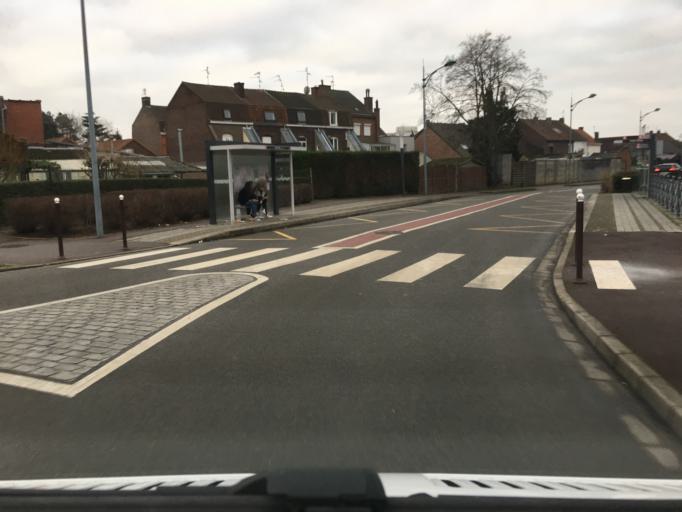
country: FR
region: Nord-Pas-de-Calais
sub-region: Departement du Nord
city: Comines
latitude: 50.7619
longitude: 3.0115
